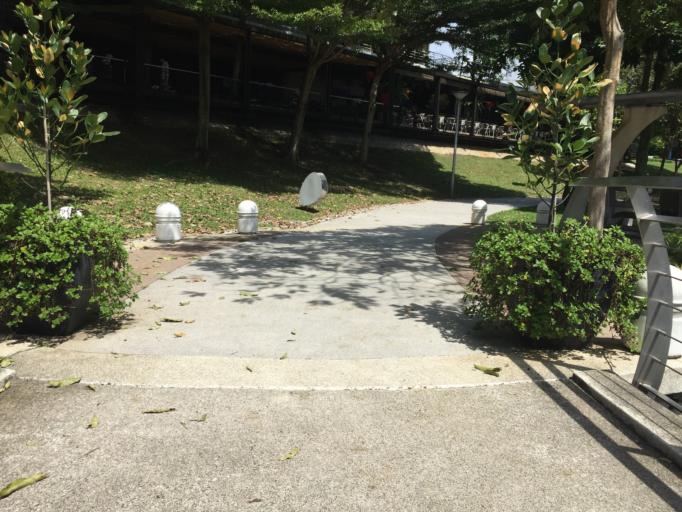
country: MY
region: Kuala Lumpur
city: Kuala Lumpur
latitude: 3.1866
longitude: 101.6283
